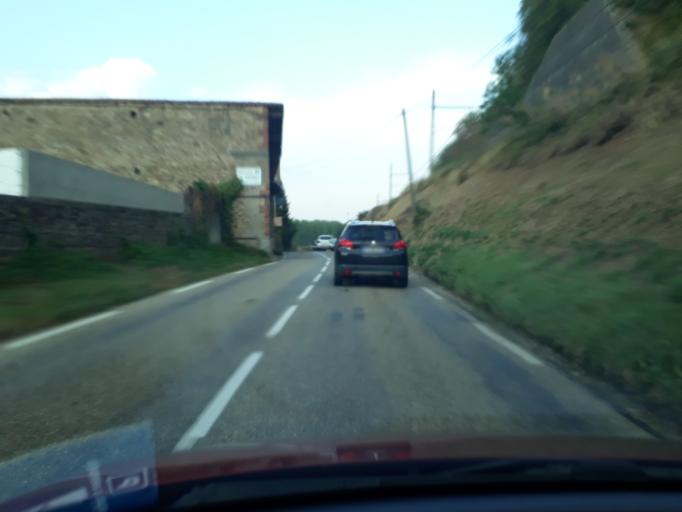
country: FR
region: Rhone-Alpes
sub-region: Departement du Rhone
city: Ampuis
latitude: 45.4725
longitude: 4.7931
